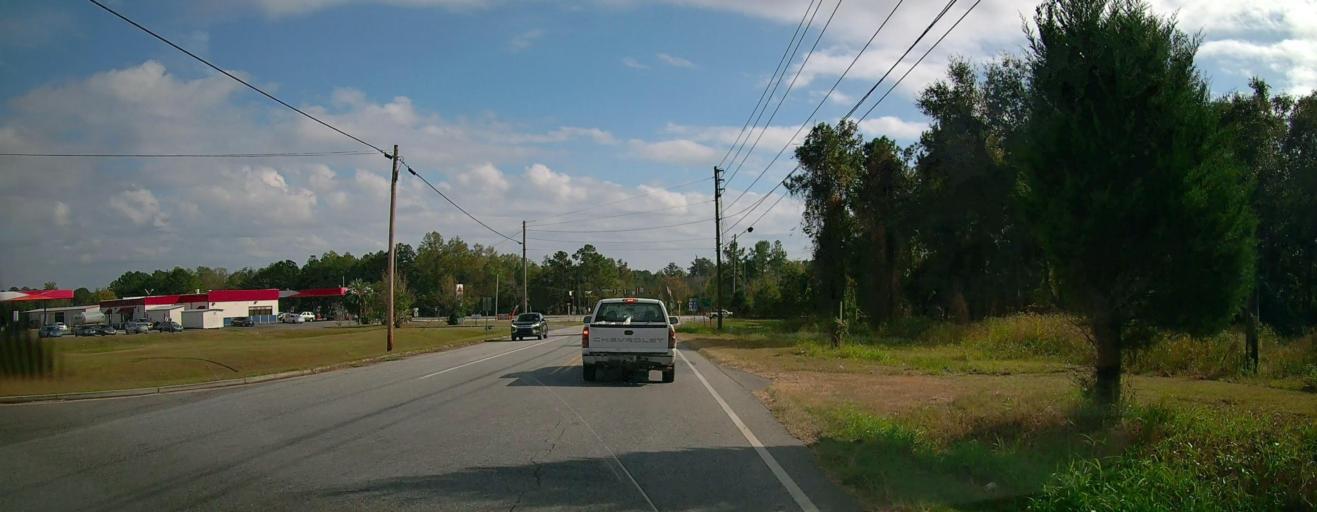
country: US
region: Georgia
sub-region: Thomas County
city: Thomasville
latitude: 30.8702
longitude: -84.0011
